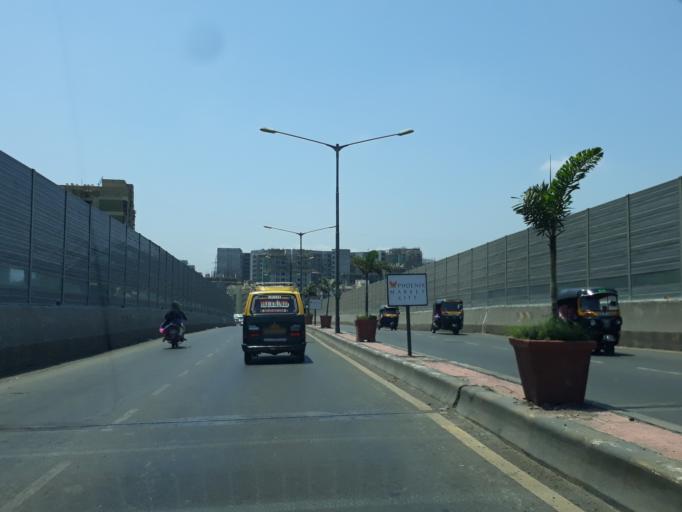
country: IN
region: Maharashtra
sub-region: Mumbai Suburban
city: Mumbai
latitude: 19.0674
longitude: 72.8888
